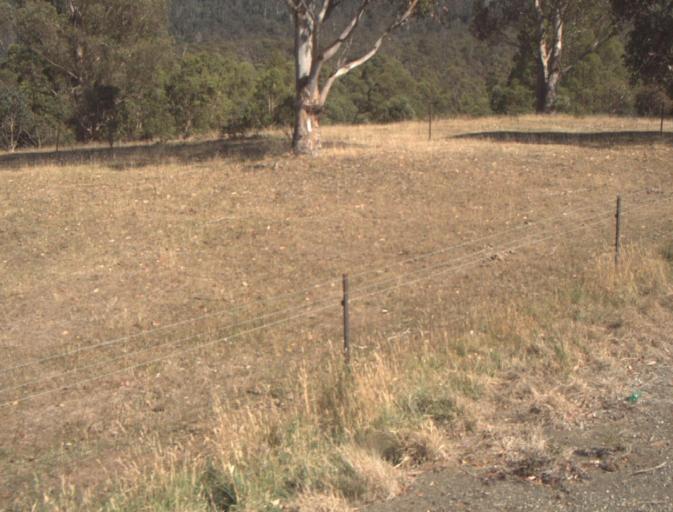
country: AU
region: Tasmania
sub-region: Launceston
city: Newstead
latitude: -41.3062
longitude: 147.3179
